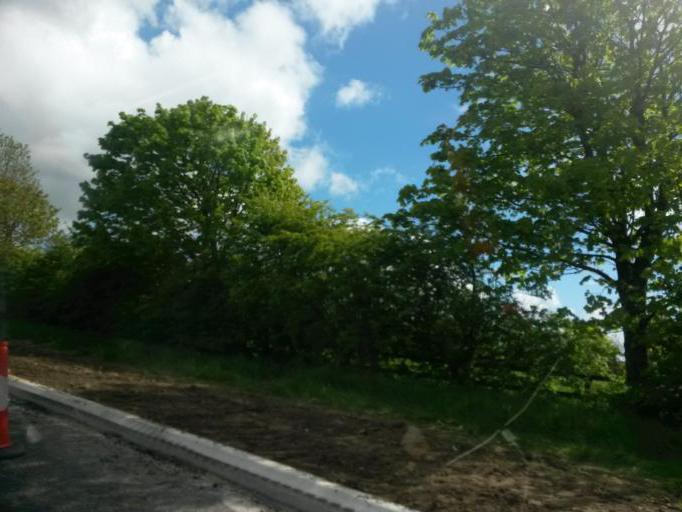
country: IE
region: Leinster
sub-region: Loch Garman
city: Castlebridge
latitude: 52.3844
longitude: -6.5181
